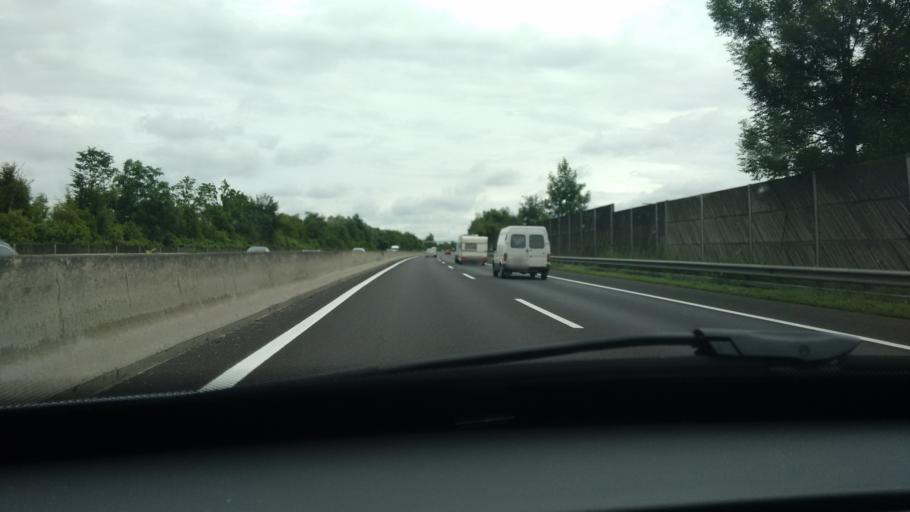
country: AT
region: Upper Austria
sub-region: Politischer Bezirk Scharding
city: Sankt Marienkirchen bei Schaerding
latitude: 48.3121
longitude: 13.4281
